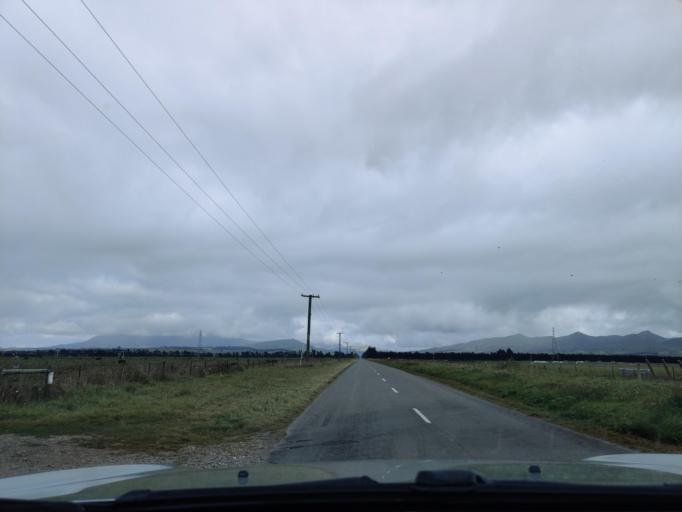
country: NZ
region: Canterbury
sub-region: Hurunui District
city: Amberley
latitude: -43.0776
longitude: 172.7273
